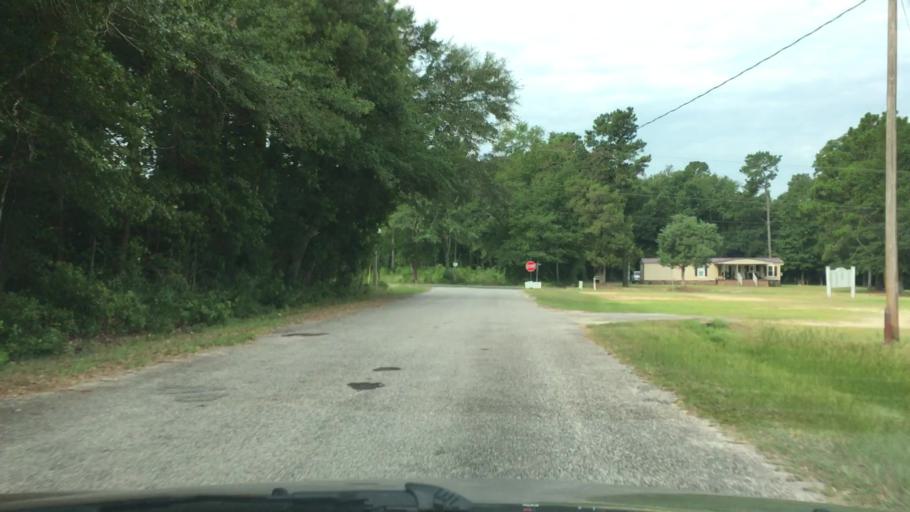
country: US
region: South Carolina
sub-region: Barnwell County
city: Williston
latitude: 33.6572
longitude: -81.3686
